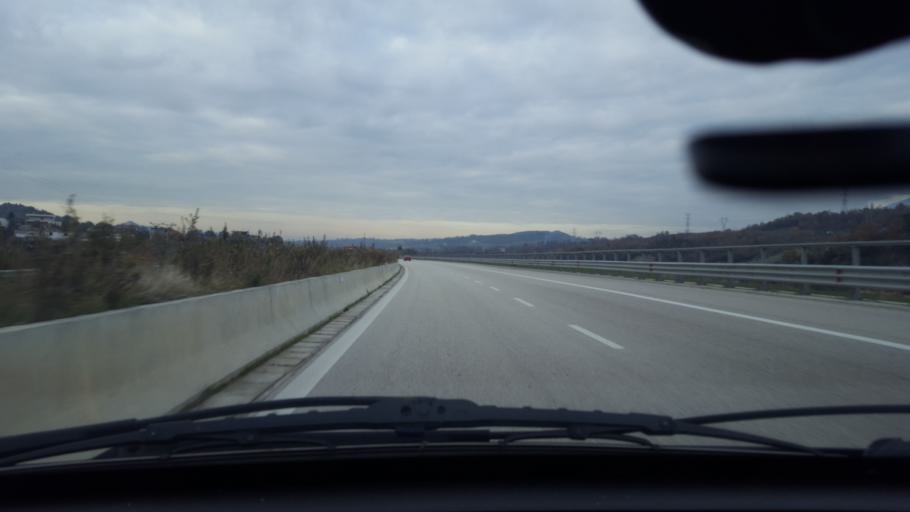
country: AL
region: Tirane
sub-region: Rrethi i Tiranes
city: Berzhite
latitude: 41.2431
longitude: 19.9118
